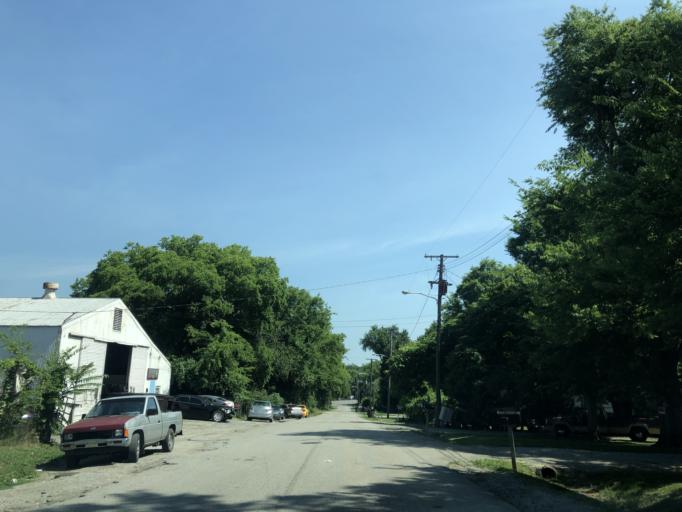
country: US
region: Tennessee
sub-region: Davidson County
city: Nashville
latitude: 36.2030
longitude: -86.7677
